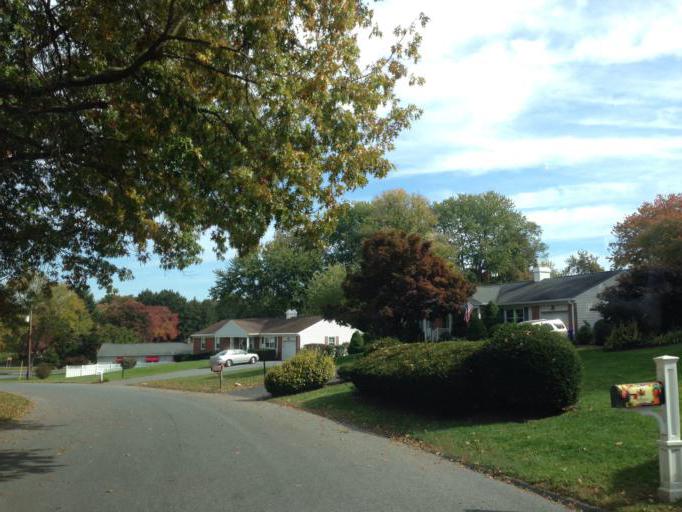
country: US
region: Maryland
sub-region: Howard County
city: Ellicott City
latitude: 39.2831
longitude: -76.8341
